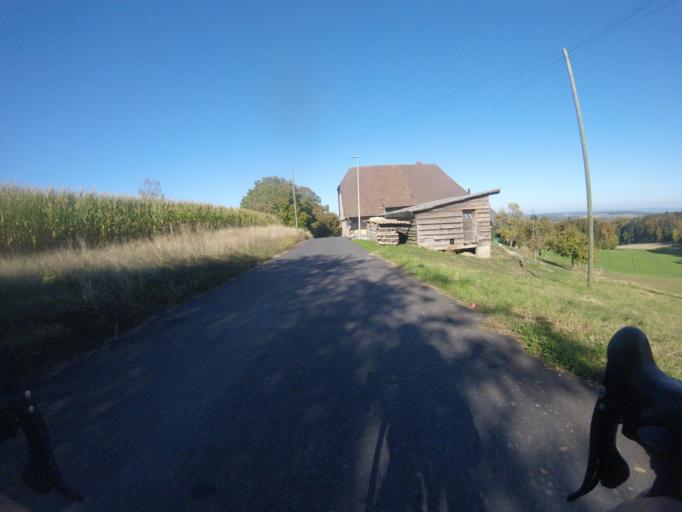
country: CH
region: Bern
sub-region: Seeland District
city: Schupfen
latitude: 47.0336
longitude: 7.3453
